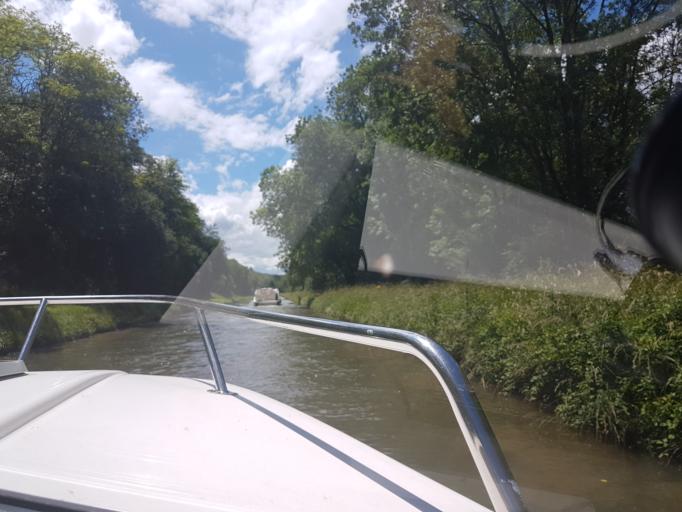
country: FR
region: Bourgogne
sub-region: Departement de l'Yonne
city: Vermenton
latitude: 47.5929
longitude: 3.6660
